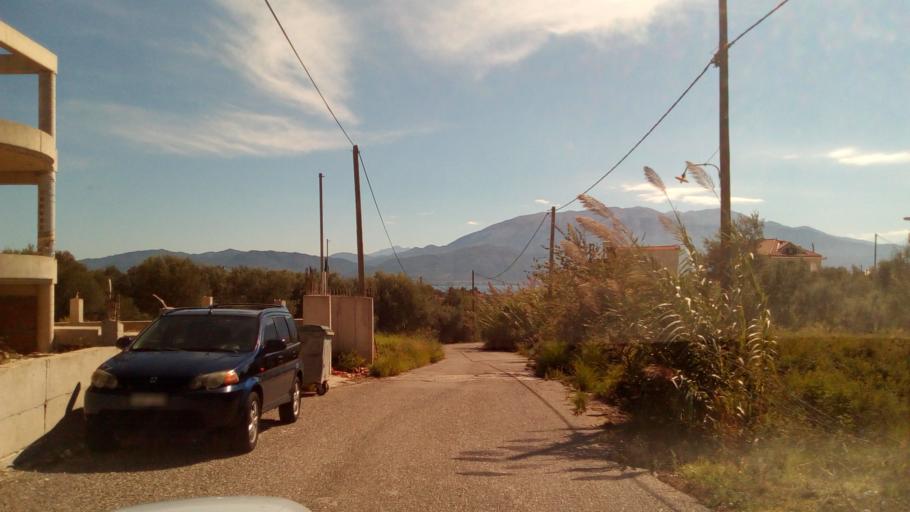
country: GR
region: West Greece
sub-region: Nomos Aitolias kai Akarnanias
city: Antirrio
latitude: 38.3703
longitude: 21.7734
